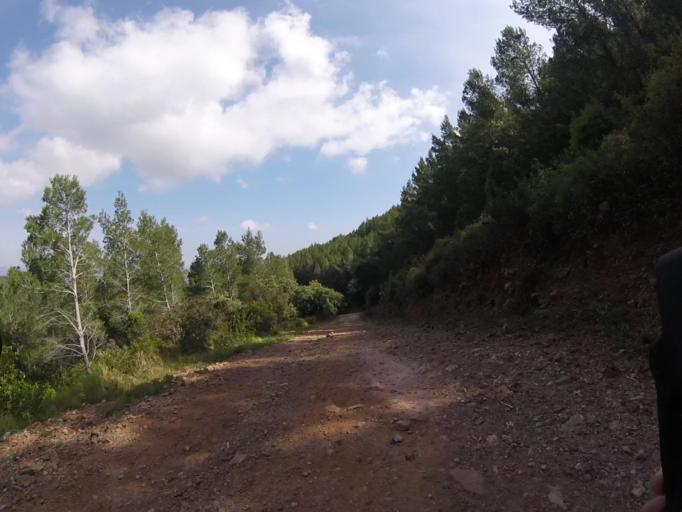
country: ES
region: Valencia
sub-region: Provincia de Castello
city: Benicassim
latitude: 40.0990
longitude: 0.0404
